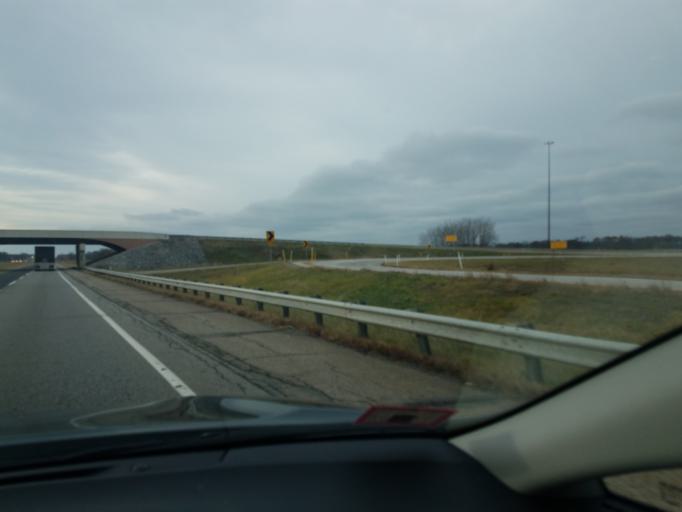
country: US
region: Michigan
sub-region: Saint Joseph County
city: Sturgis
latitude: 41.7539
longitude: -85.4319
